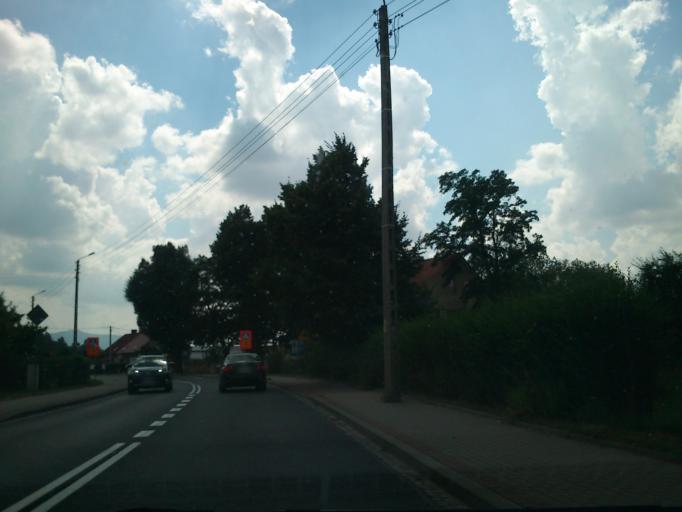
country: PL
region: Lower Silesian Voivodeship
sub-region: Powiat wroclawski
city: Gniechowice
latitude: 50.9557
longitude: 16.7825
